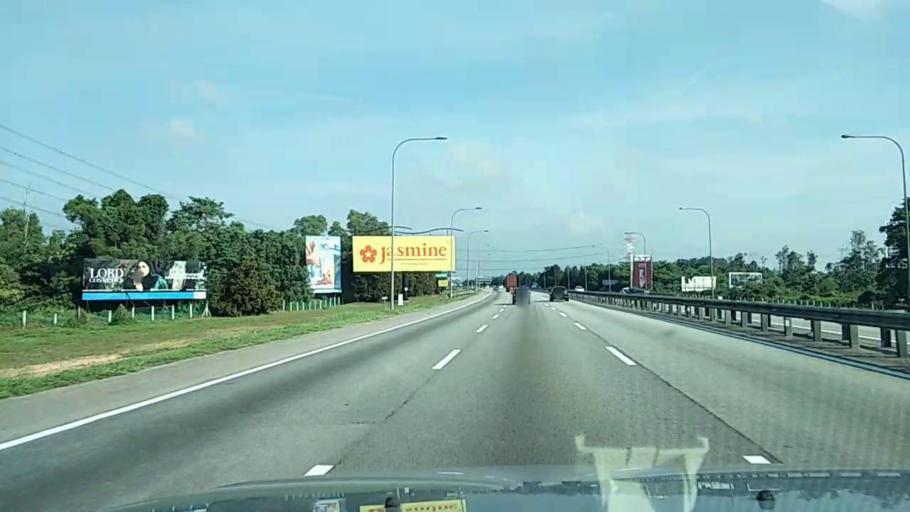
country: MY
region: Putrajaya
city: Putrajaya
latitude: 2.8718
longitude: 101.6360
